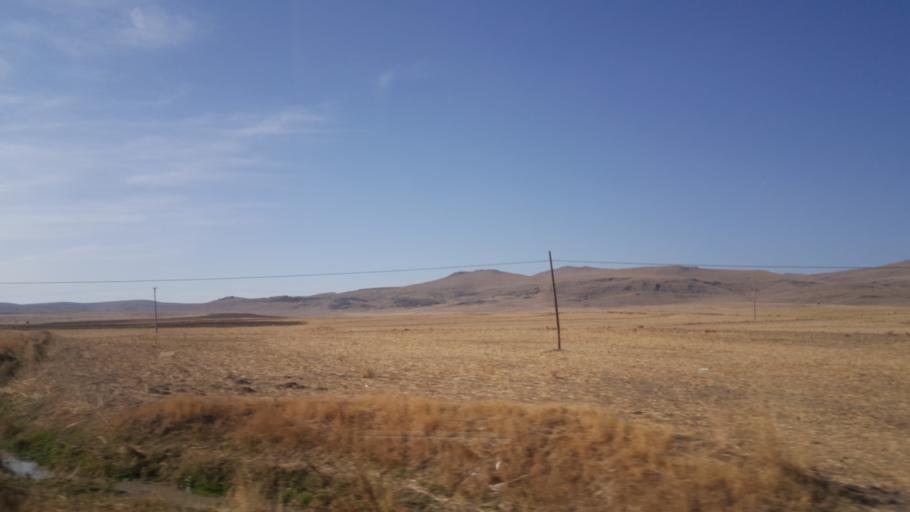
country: TR
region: Ankara
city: Altpinar
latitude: 39.2531
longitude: 32.7521
